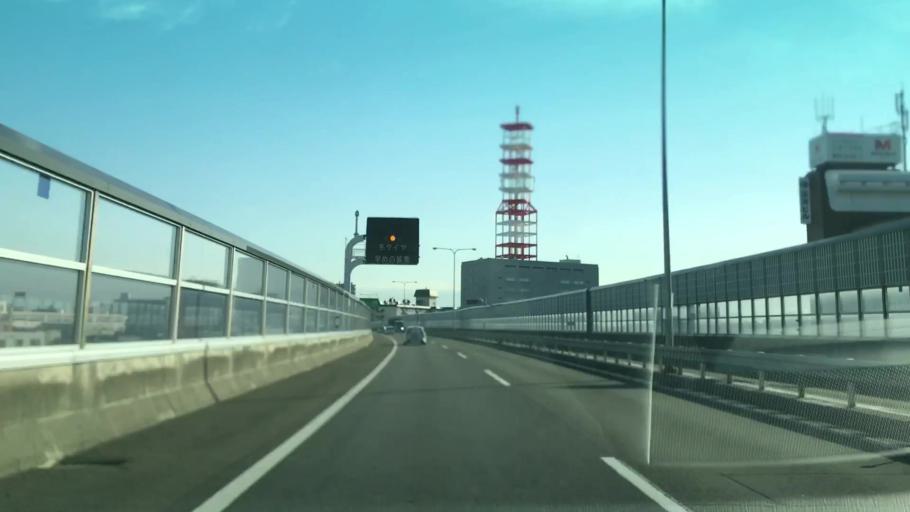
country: JP
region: Hokkaido
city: Sapporo
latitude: 43.1005
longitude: 141.3307
